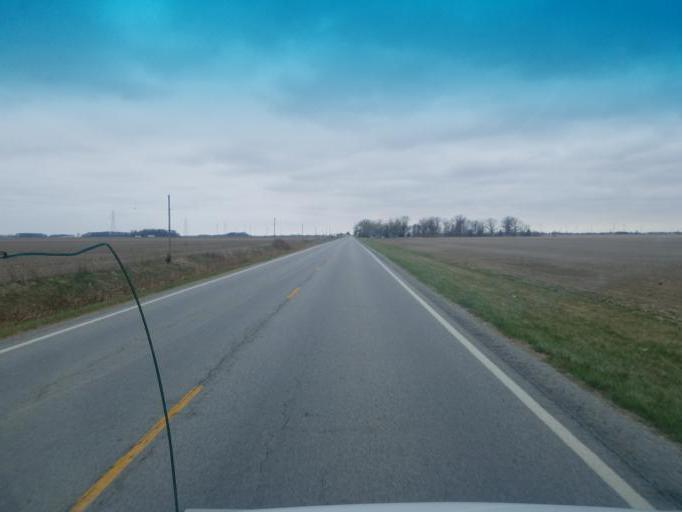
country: US
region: Ohio
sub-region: Van Wert County
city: Van Wert
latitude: 40.9321
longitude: -84.4630
